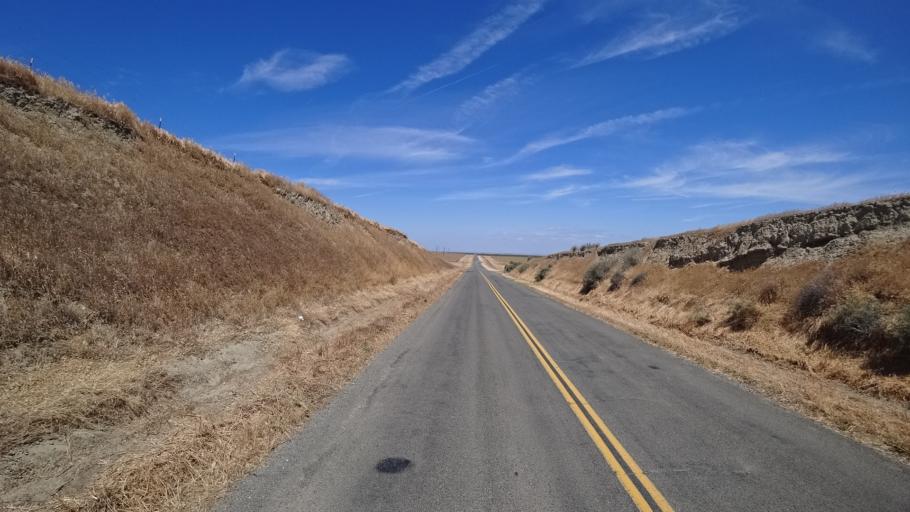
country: US
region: California
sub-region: Kings County
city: Kettleman City
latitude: 35.8957
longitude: -119.9151
